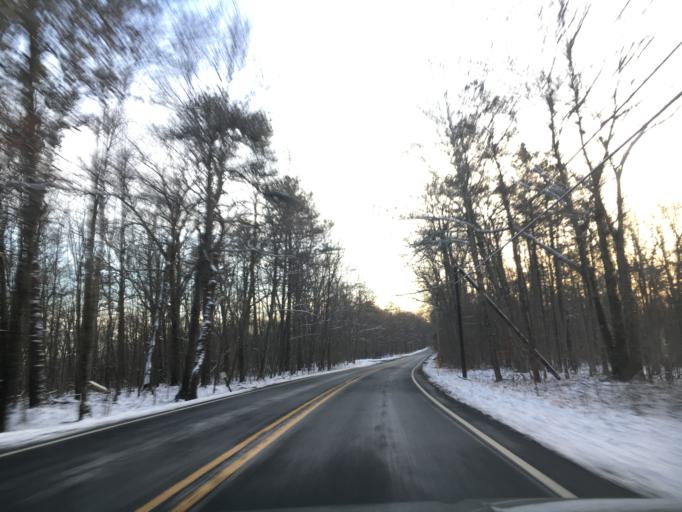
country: US
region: Pennsylvania
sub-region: Pike County
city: Saw Creek
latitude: 41.1490
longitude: -75.0803
